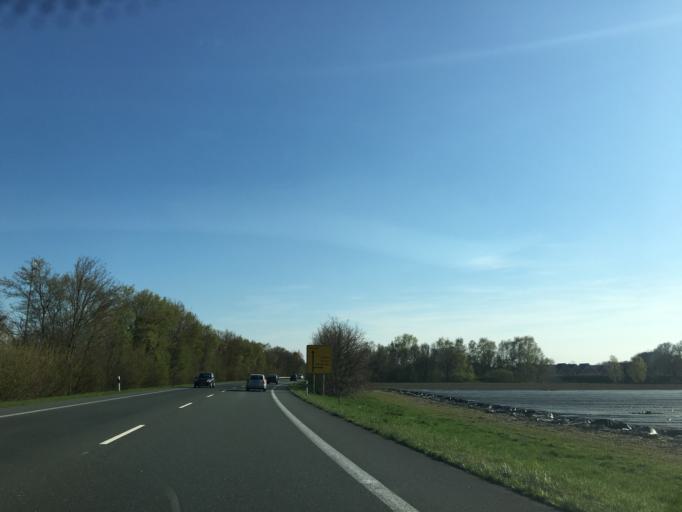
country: DE
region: North Rhine-Westphalia
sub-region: Regierungsbezirk Munster
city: Muenster
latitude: 52.0284
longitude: 7.6815
